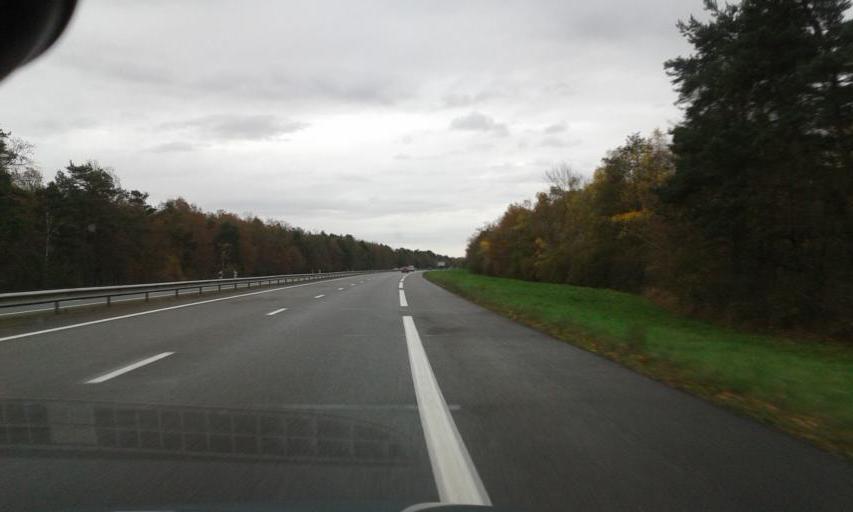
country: FR
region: Centre
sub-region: Departement du Loiret
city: Chateauneuf-sur-Loire
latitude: 47.9033
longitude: 2.1958
